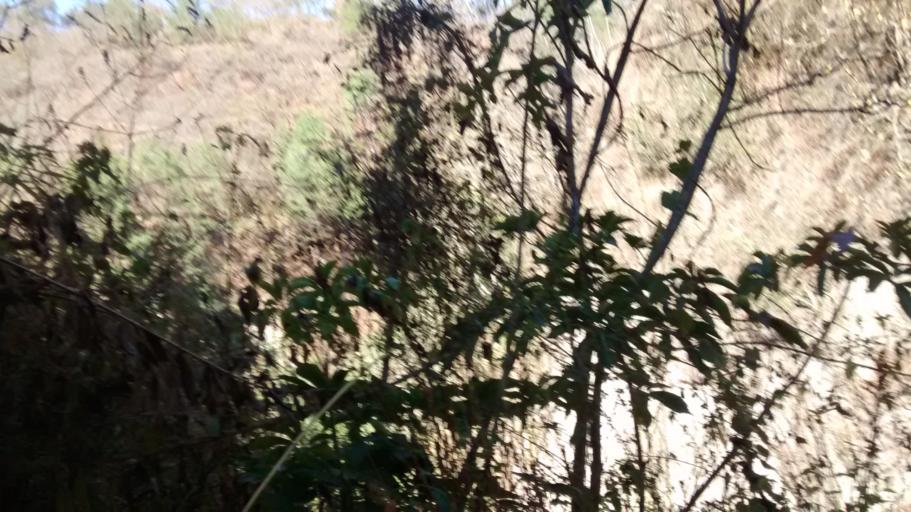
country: GT
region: Sacatepequez
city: Santo Domingo Xenacoj
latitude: 14.6800
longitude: -90.7216
